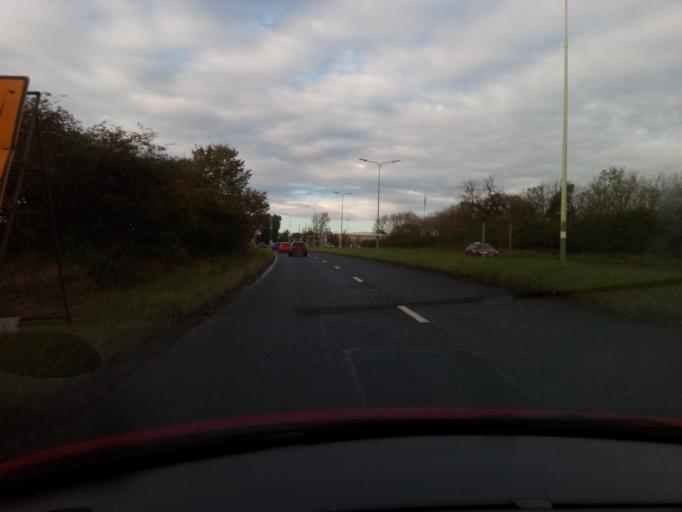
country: GB
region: England
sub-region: Darlington
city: Heighington
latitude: 54.5604
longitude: -1.5968
